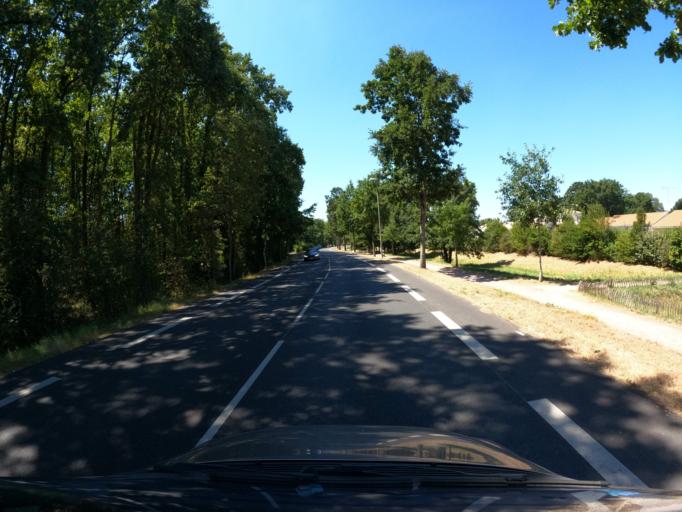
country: FR
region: Pays de la Loire
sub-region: Departement de la Vendee
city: Challans
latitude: 46.8389
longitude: -1.8875
